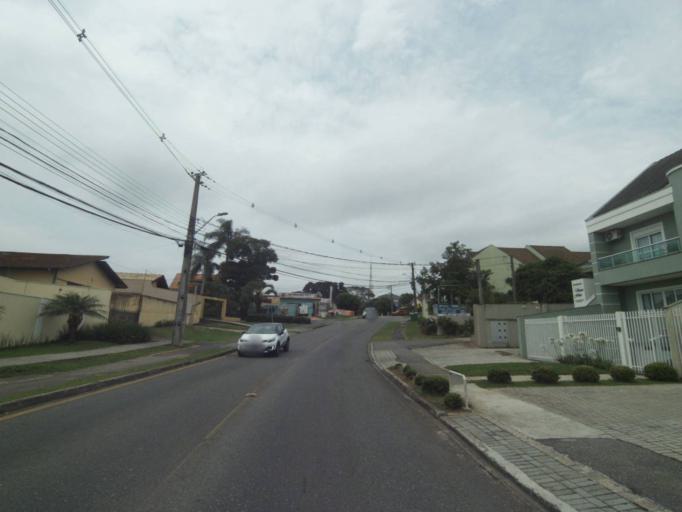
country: BR
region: Parana
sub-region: Curitiba
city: Curitiba
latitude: -25.4141
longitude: -49.2945
